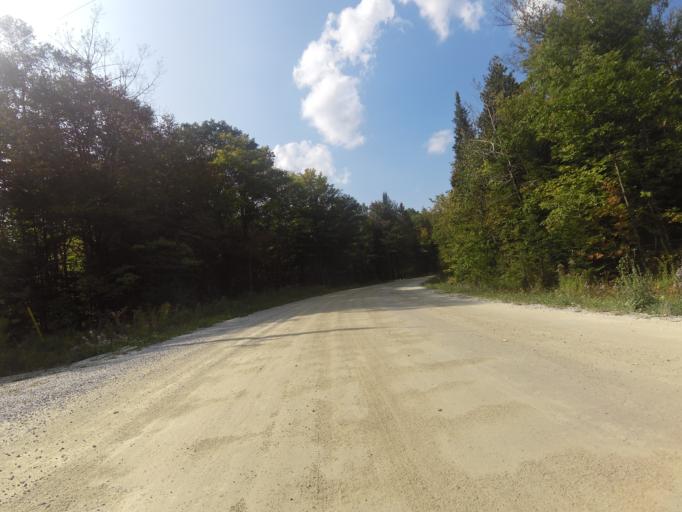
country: CA
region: Ontario
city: Renfrew
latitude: 45.1486
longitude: -76.6774
